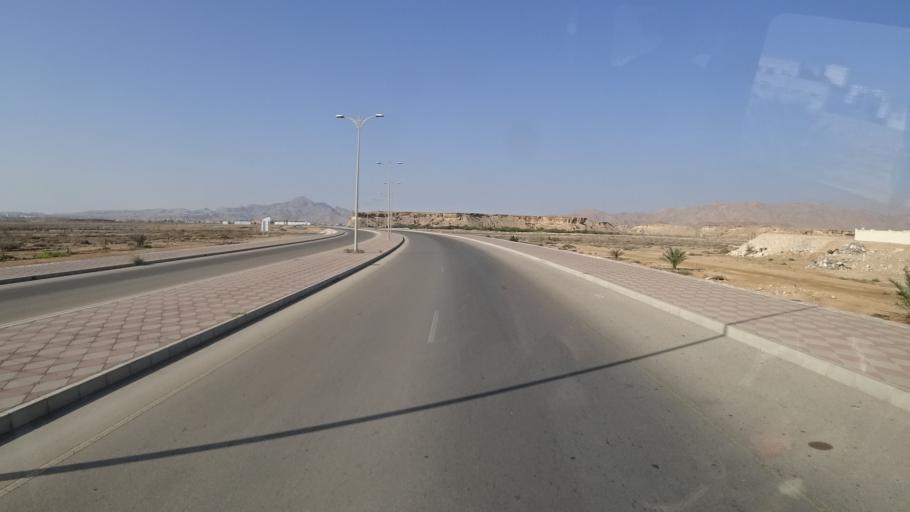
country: OM
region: Ash Sharqiyah
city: Sur
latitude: 22.5986
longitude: 59.4802
